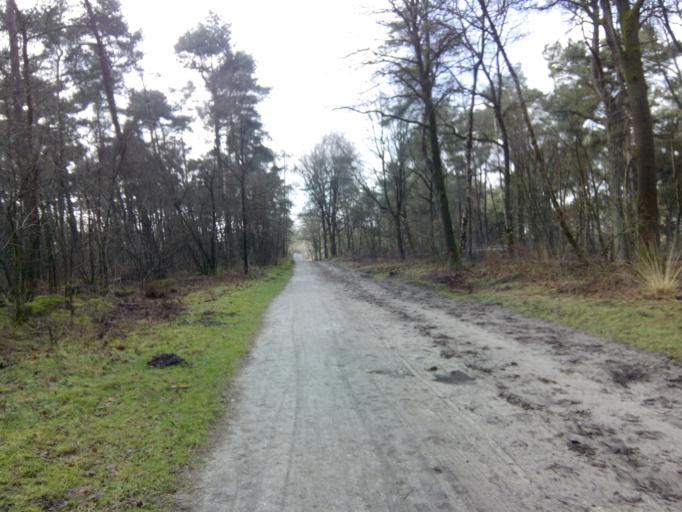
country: NL
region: Utrecht
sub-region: Gemeente Utrechtse Heuvelrug
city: Leersum
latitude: 52.0375
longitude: 5.4433
